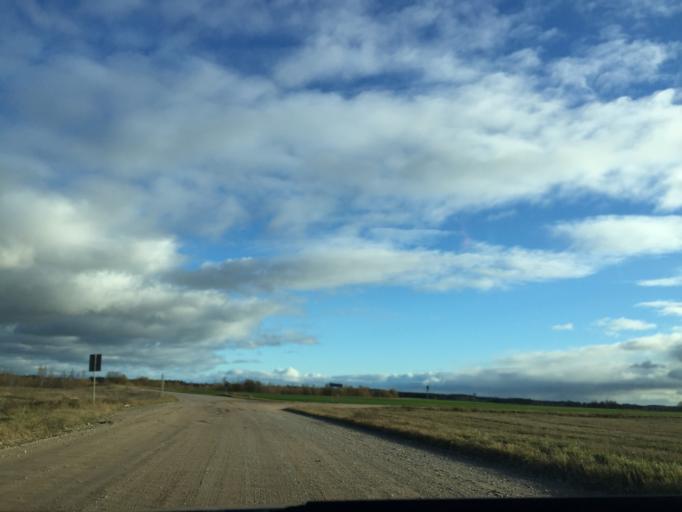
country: LV
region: Kandava
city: Kandava
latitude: 56.9600
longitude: 22.9404
